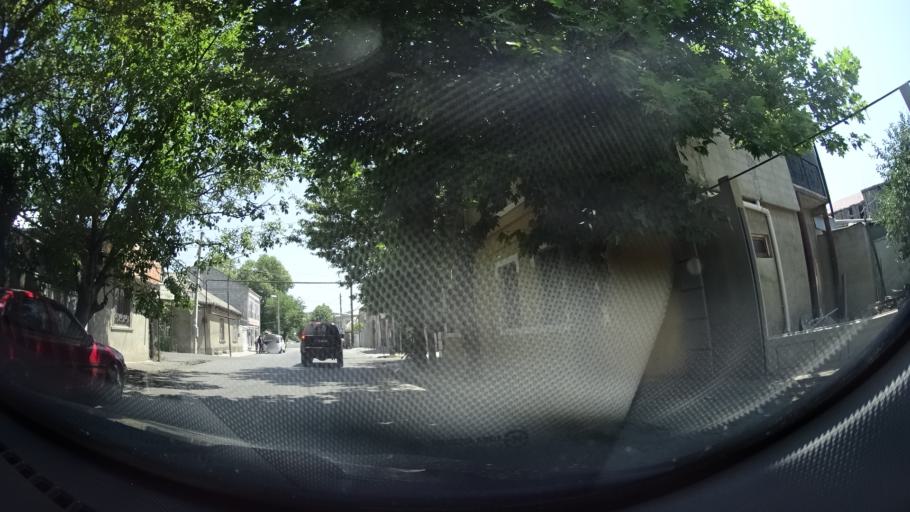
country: GE
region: Shida Kartli
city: Gori
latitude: 41.9889
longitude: 44.1147
